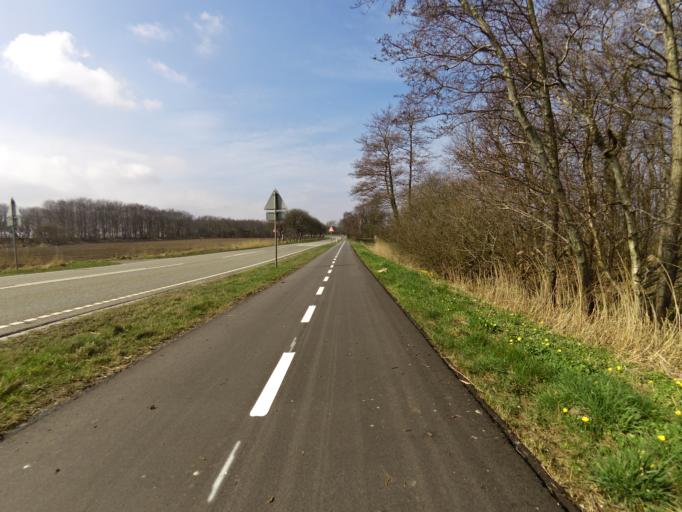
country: DK
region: Central Jutland
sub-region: Struer Kommune
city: Struer
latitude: 56.4752
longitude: 8.6175
